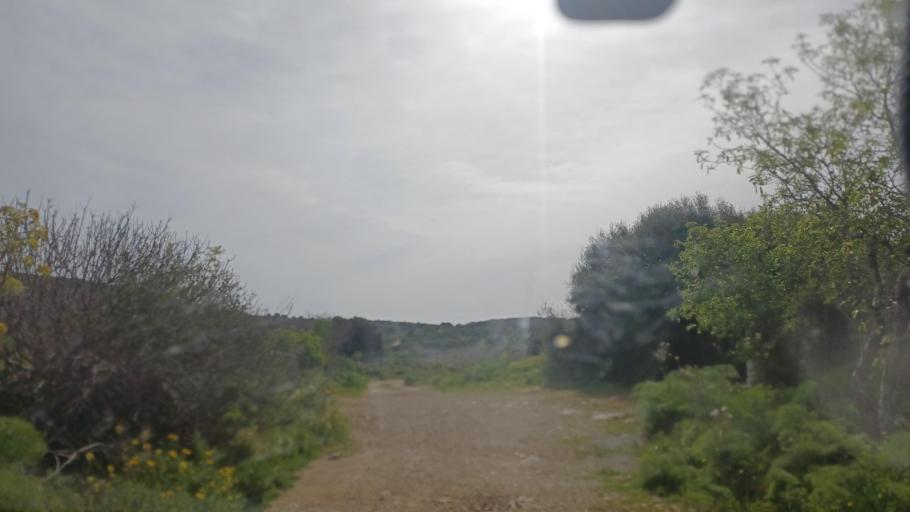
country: CY
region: Pafos
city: Mesogi
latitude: 34.7825
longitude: 32.4689
